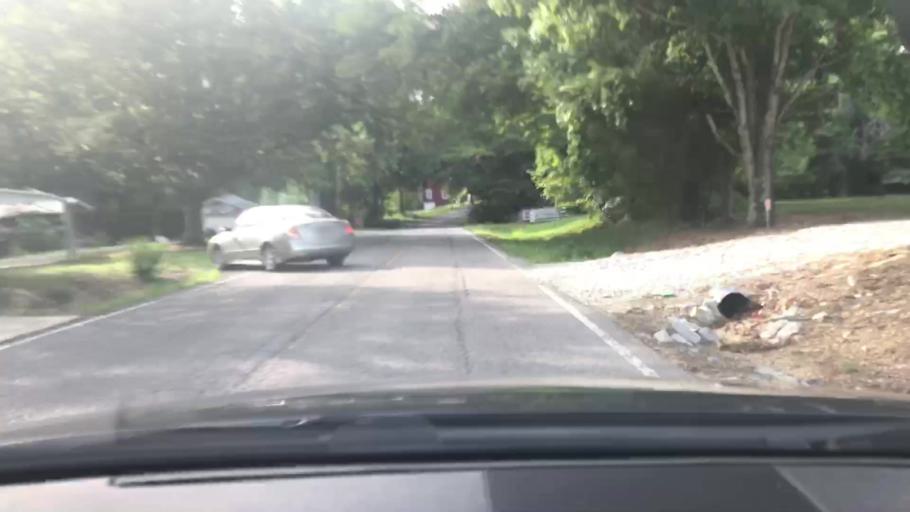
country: US
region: Tennessee
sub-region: Dickson County
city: White Bluff
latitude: 36.1601
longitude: -87.2569
